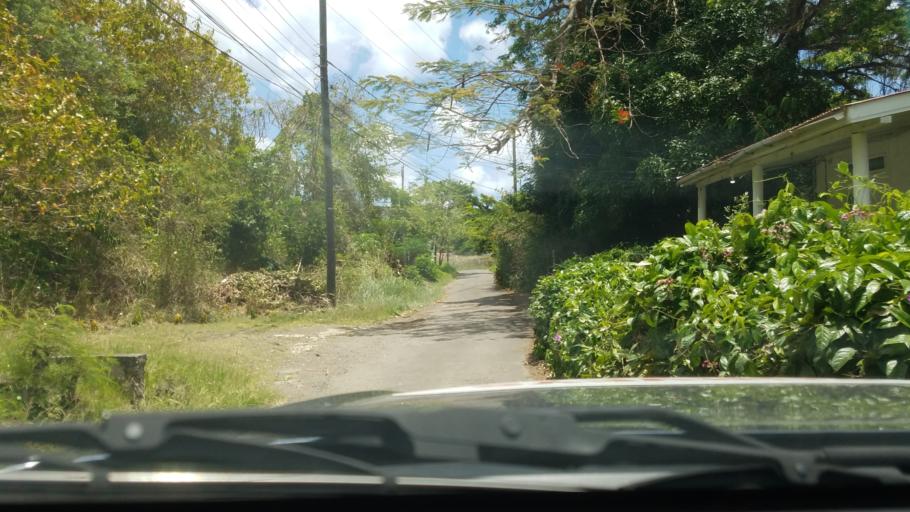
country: LC
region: Castries Quarter
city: Bisee
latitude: 14.0173
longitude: -60.9967
